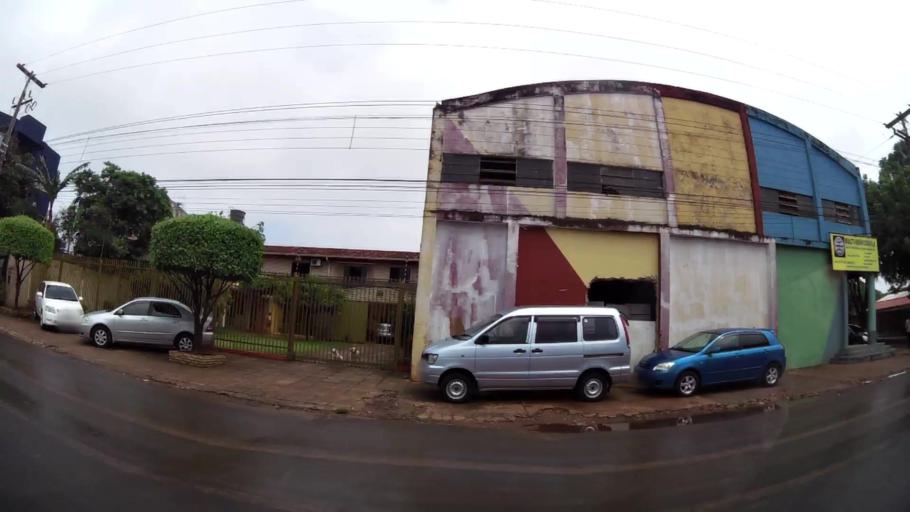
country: PY
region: Alto Parana
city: Ciudad del Este
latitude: -25.5067
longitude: -54.6602
